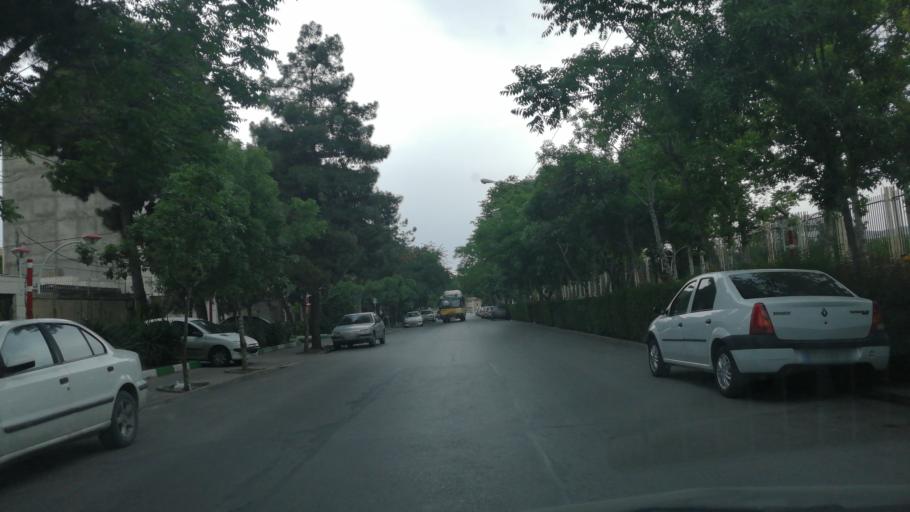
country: IR
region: Razavi Khorasan
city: Mashhad
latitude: 36.2876
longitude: 59.5817
